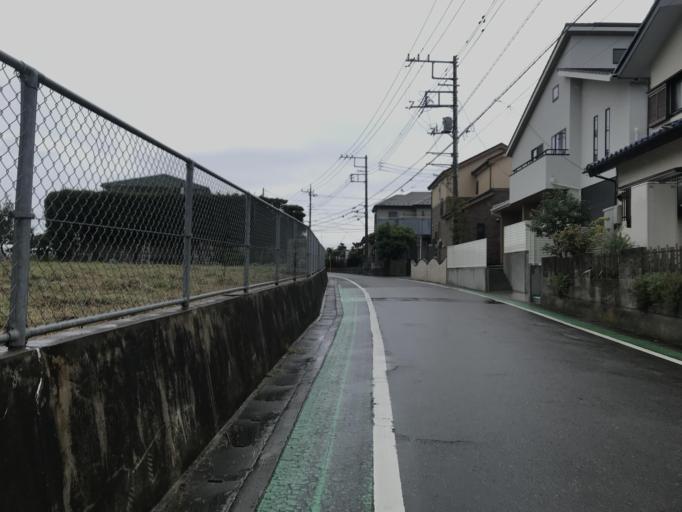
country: JP
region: Kanagawa
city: Zama
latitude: 35.5524
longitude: 139.3296
